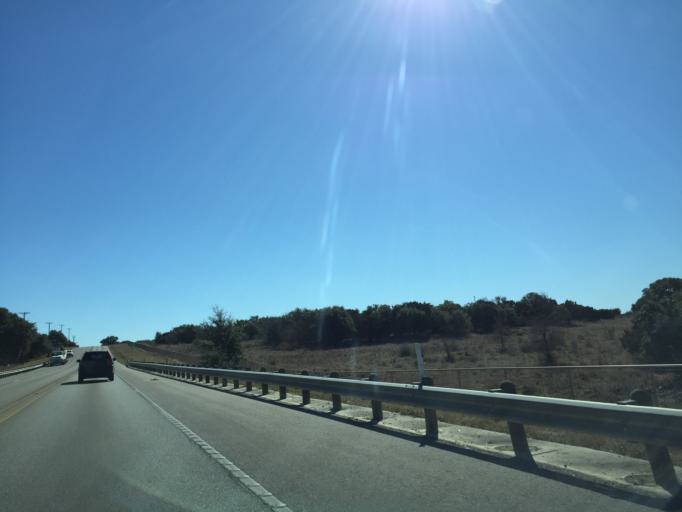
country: US
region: Texas
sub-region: Comal County
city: Canyon Lake
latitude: 29.7769
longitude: -98.3096
